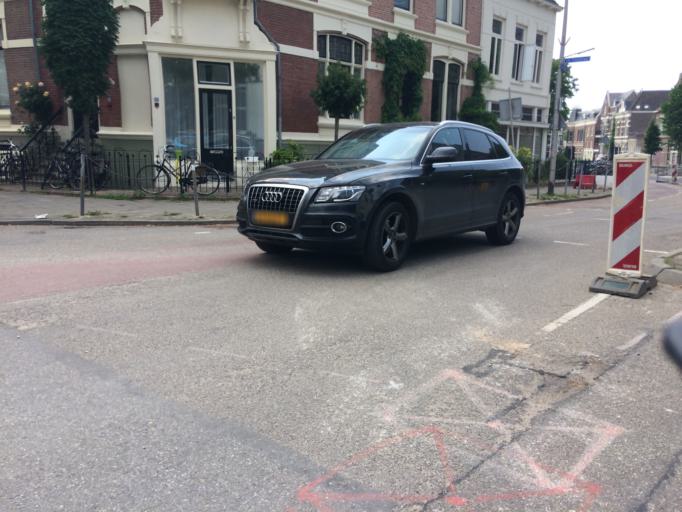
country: NL
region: Gelderland
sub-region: Gemeente Nijmegen
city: Nijmegen
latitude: 51.8399
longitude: 5.8589
